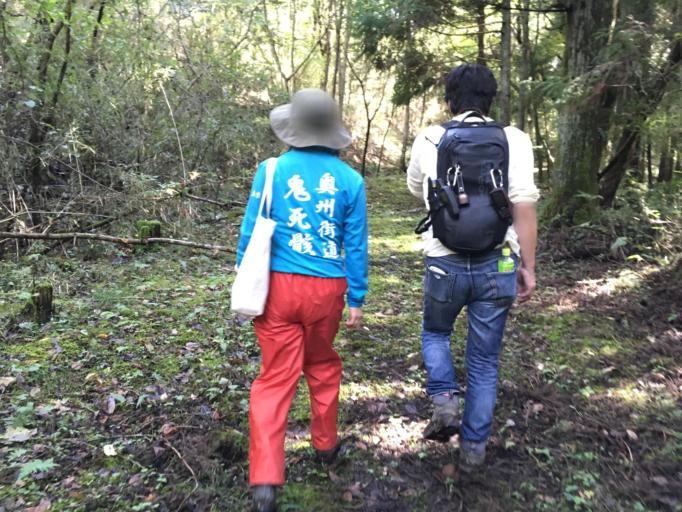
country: JP
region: Iwate
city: Ichinoseki
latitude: 38.8746
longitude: 141.1254
